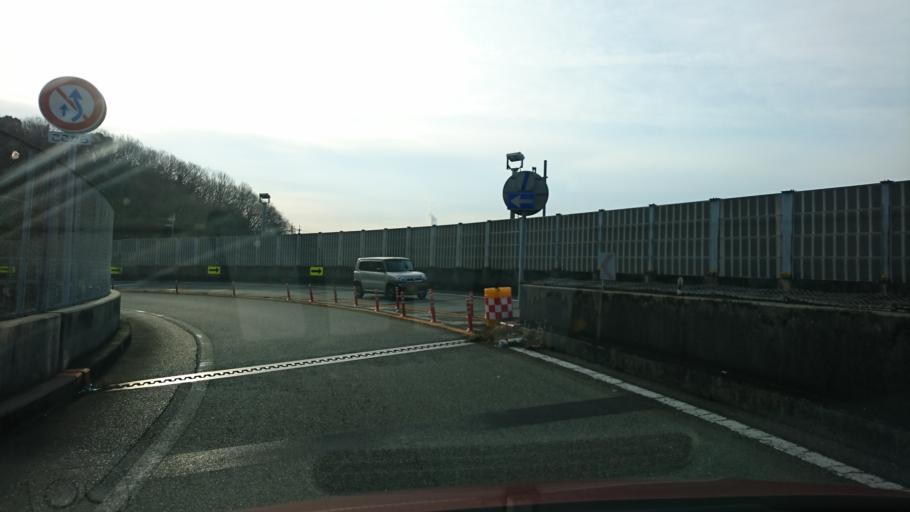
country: JP
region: Hyogo
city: Shirahamacho-usazakiminami
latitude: 34.7991
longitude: 134.7418
